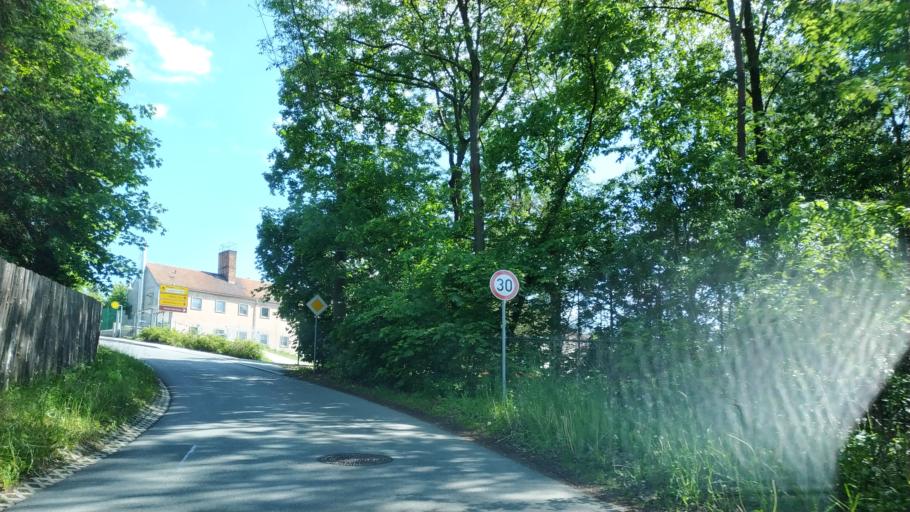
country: DE
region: Saxony
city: Pohl
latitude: 50.5610
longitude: 12.1714
